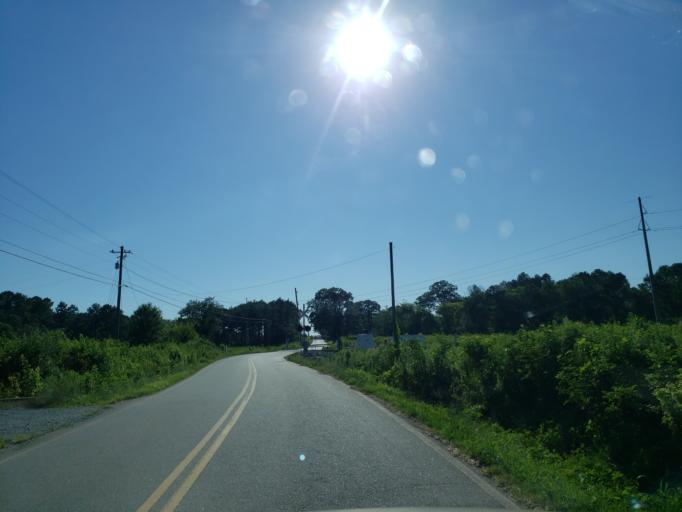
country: US
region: Georgia
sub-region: Bartow County
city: Euharlee
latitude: 34.1085
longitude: -84.9349
